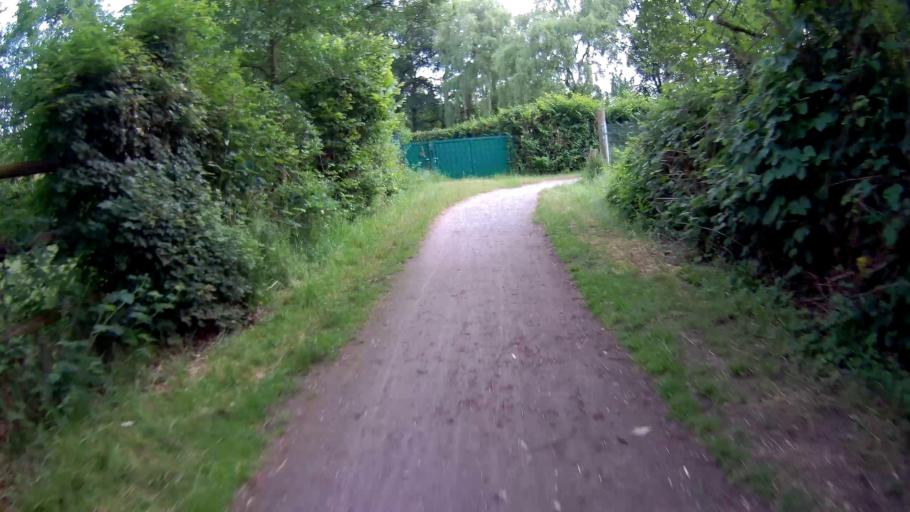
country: DE
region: North Rhine-Westphalia
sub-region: Regierungsbezirk Munster
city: Gladbeck
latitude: 51.5865
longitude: 6.9699
